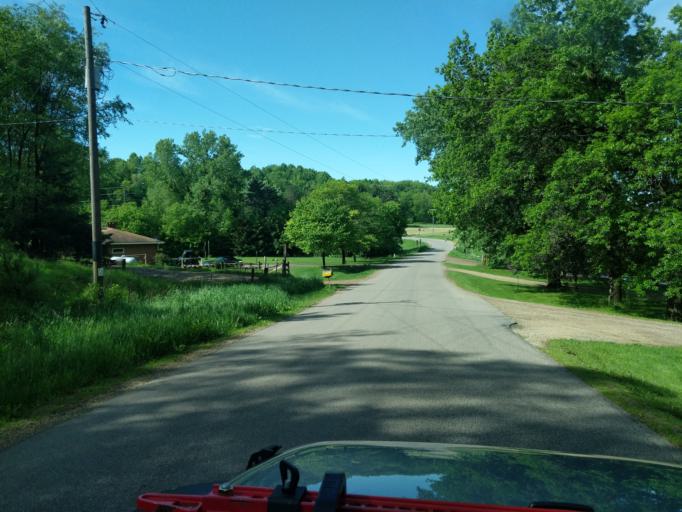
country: US
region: Wisconsin
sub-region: Pierce County
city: River Falls
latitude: 44.8607
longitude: -92.5268
